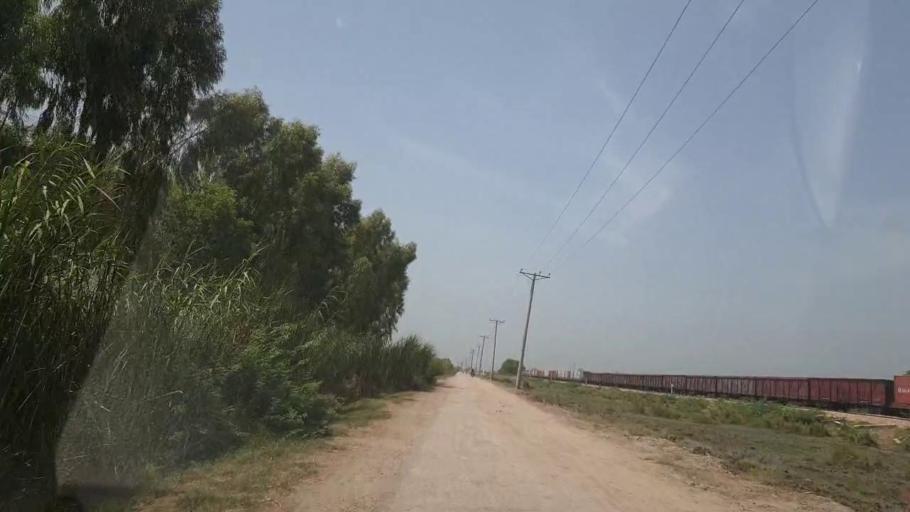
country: PK
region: Sindh
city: Gambat
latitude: 27.3277
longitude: 68.5398
